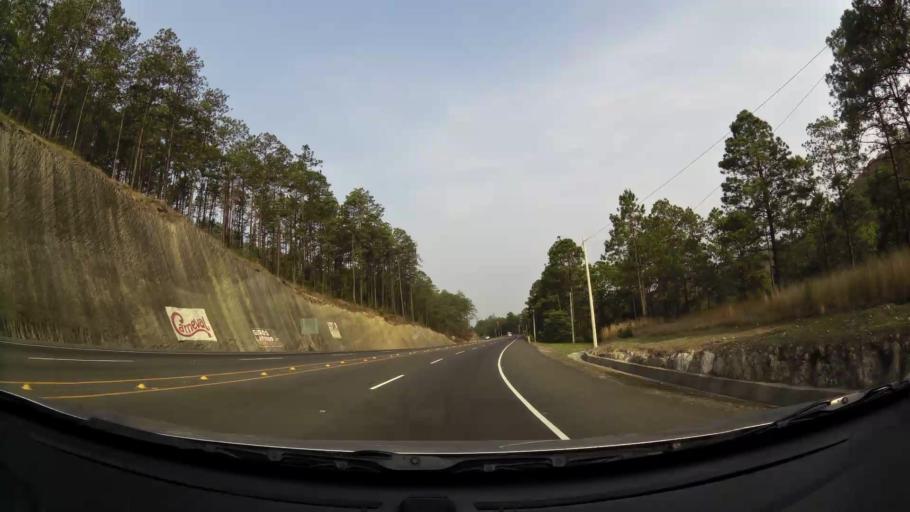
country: HN
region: Francisco Morazan
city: Zambrano
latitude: 14.2851
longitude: -87.4479
